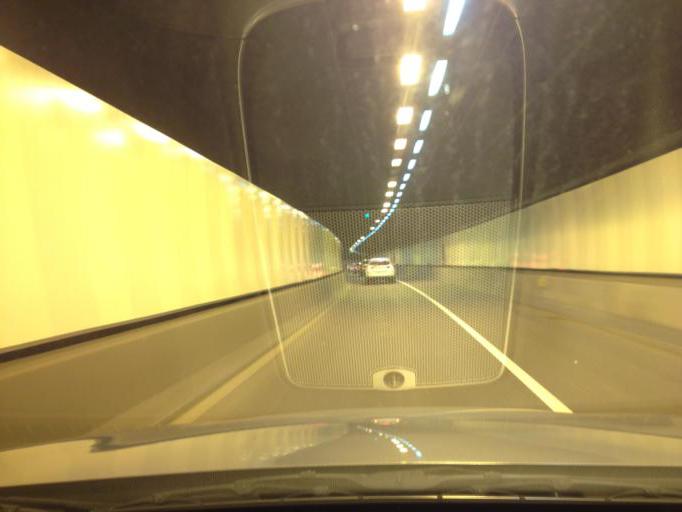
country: AU
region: New South Wales
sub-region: City of Sydney
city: Darlinghurst
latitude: -33.8853
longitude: 151.2182
